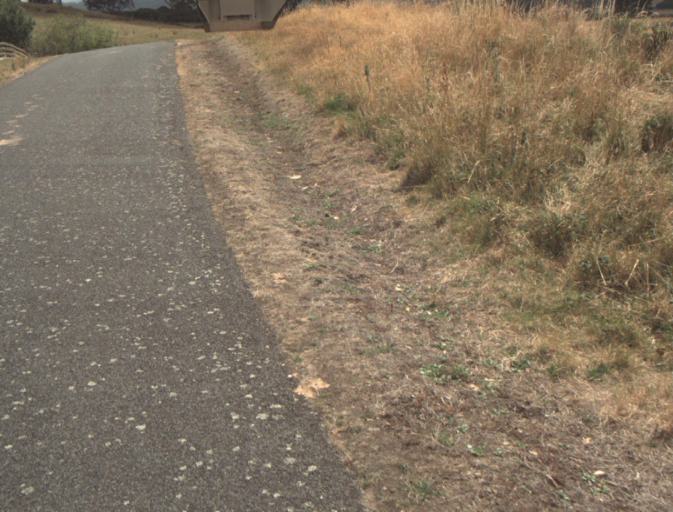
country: AU
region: Tasmania
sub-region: Northern Midlands
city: Evandale
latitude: -41.5152
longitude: 147.4713
